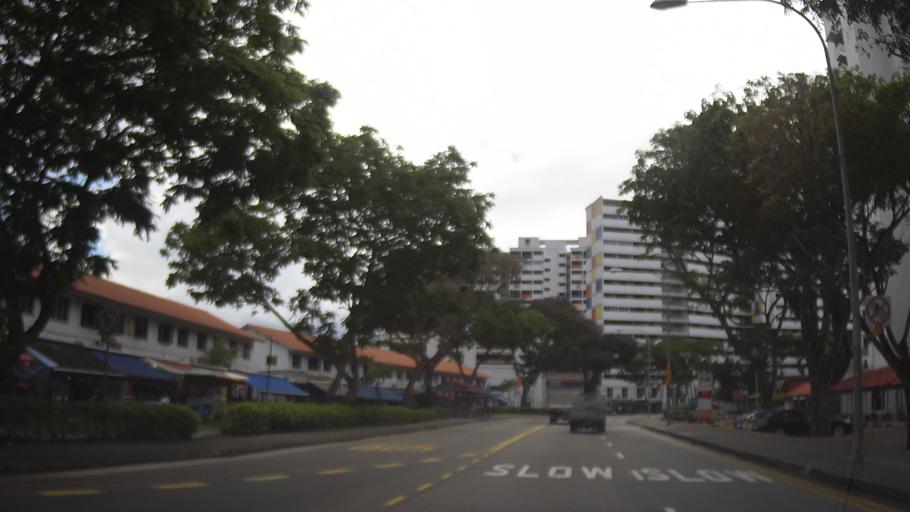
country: SG
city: Singapore
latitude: 1.3276
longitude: 103.8855
